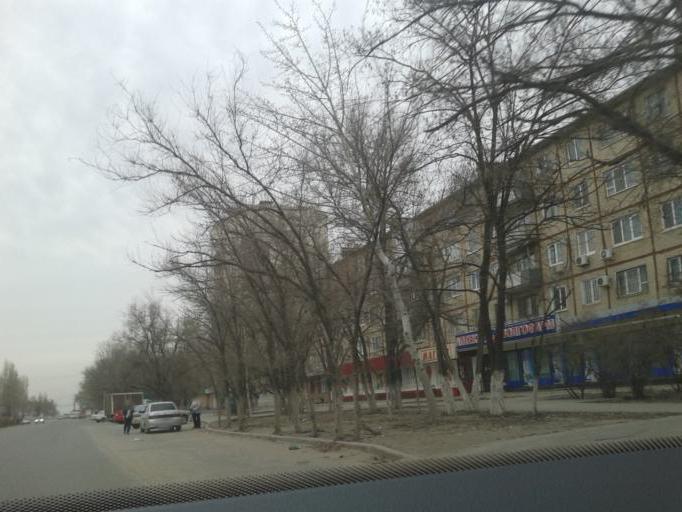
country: RU
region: Volgograd
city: Gorodishche
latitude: 48.7638
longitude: 44.4784
